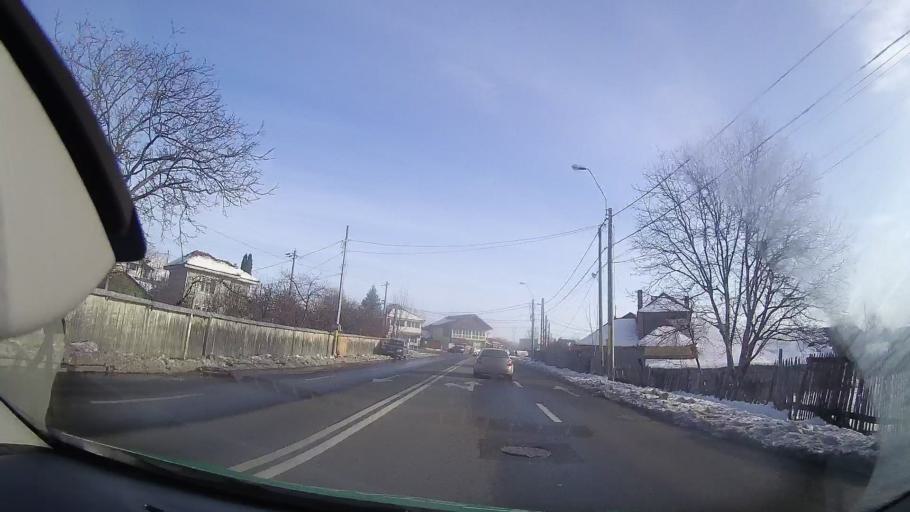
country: RO
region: Neamt
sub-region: Comuna Garcina
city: Garcina
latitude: 46.9599
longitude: 26.3810
